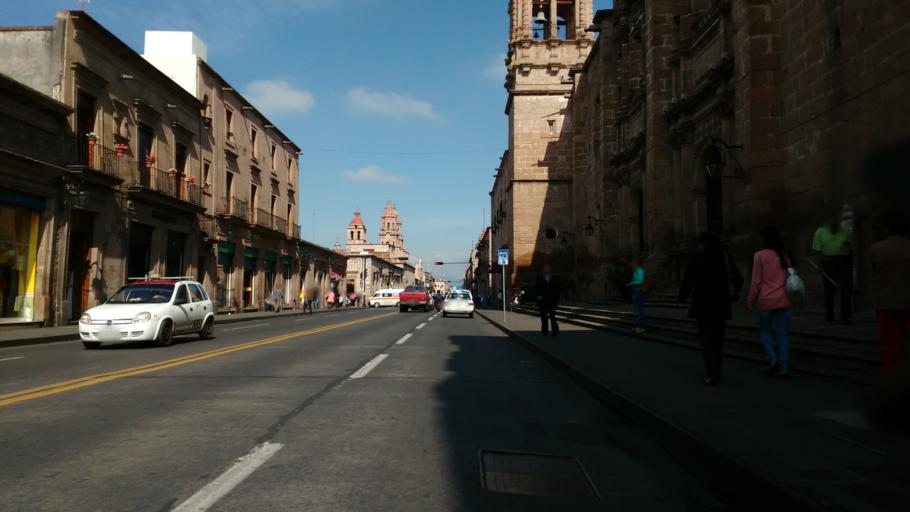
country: MX
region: Michoacan
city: Morelia
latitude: 19.7029
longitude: -101.1880
